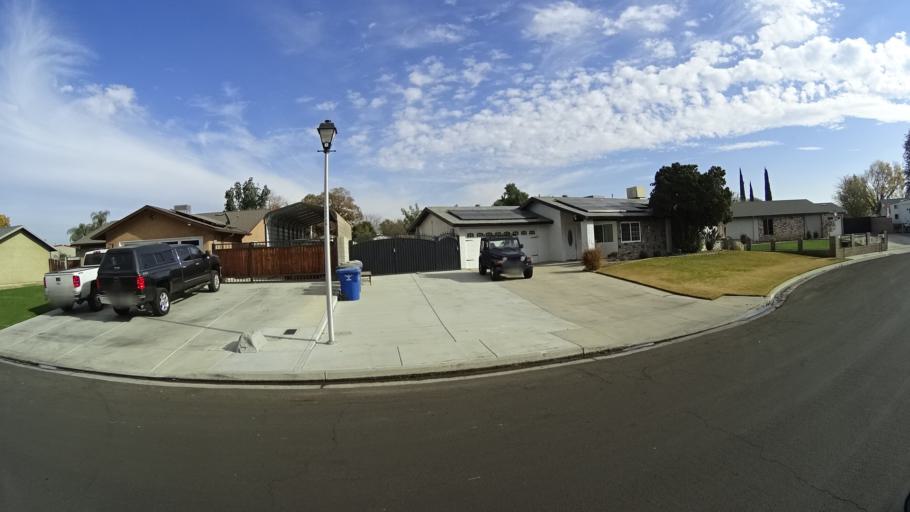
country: US
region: California
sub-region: Kern County
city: Greenacres
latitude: 35.3961
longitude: -119.1215
